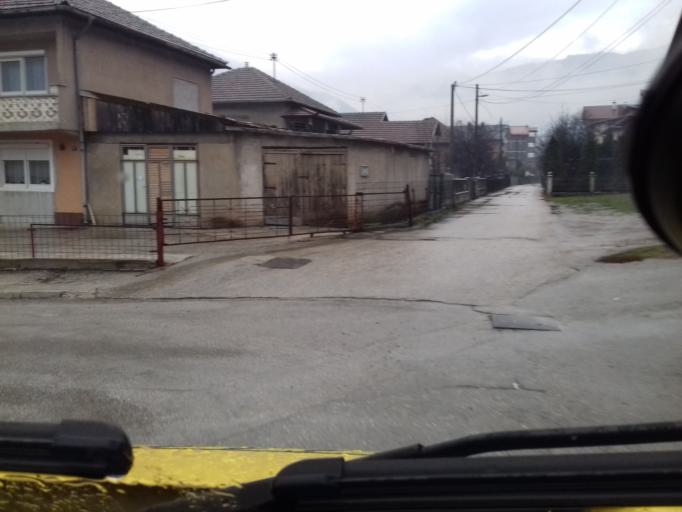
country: BA
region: Federation of Bosnia and Herzegovina
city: Zeljezno Polje
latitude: 44.3305
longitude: 17.9113
